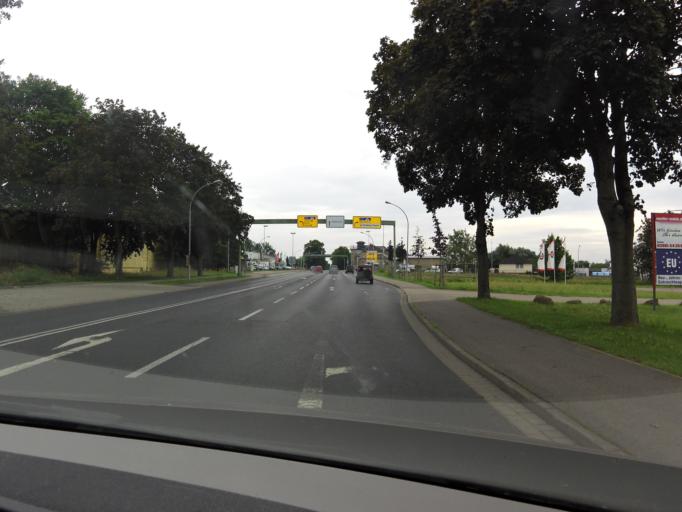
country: DE
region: Mecklenburg-Vorpommern
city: Neustrelitz
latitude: 53.3455
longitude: 13.0823
